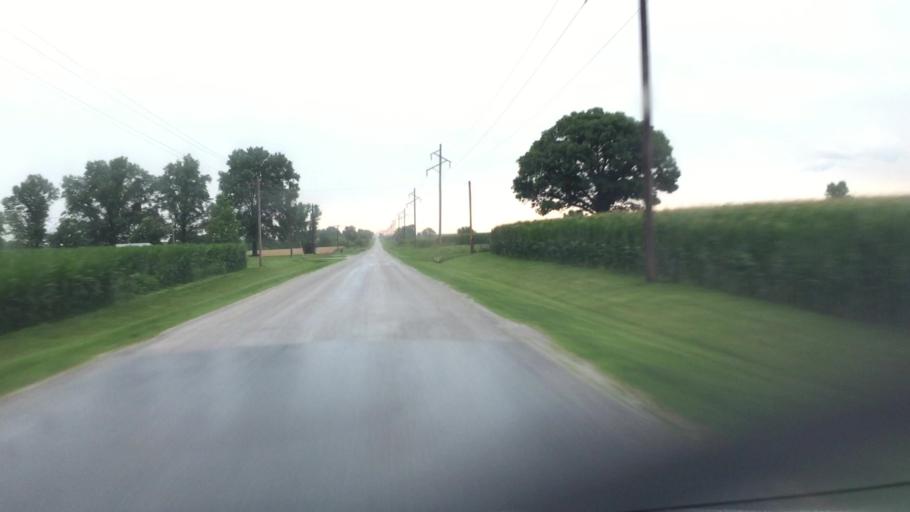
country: US
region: Illinois
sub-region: Hancock County
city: Hamilton
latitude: 40.4315
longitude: -91.2715
